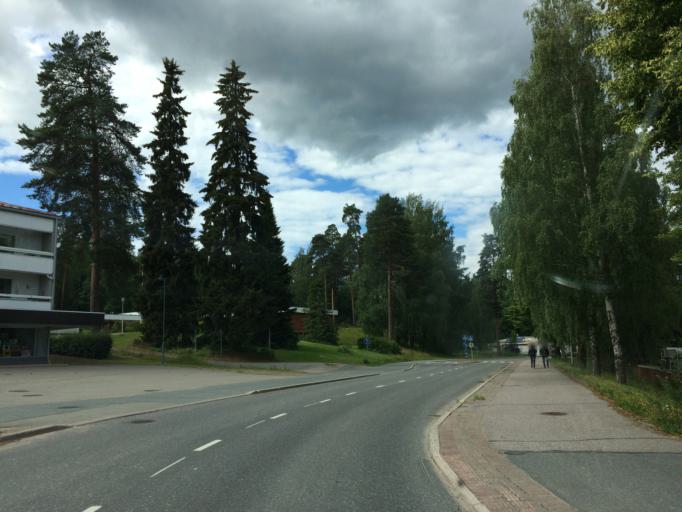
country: FI
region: Haeme
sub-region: Haemeenlinna
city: Tervakoski
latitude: 60.8162
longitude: 24.6242
